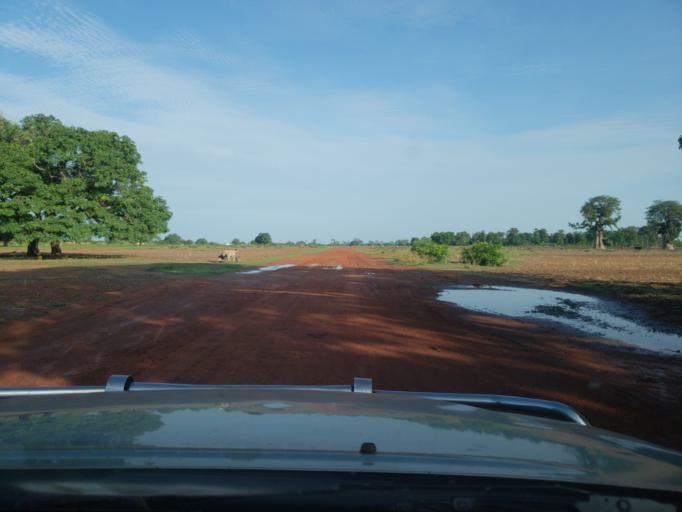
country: ML
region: Sikasso
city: Koutiala
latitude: 12.4287
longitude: -5.6041
